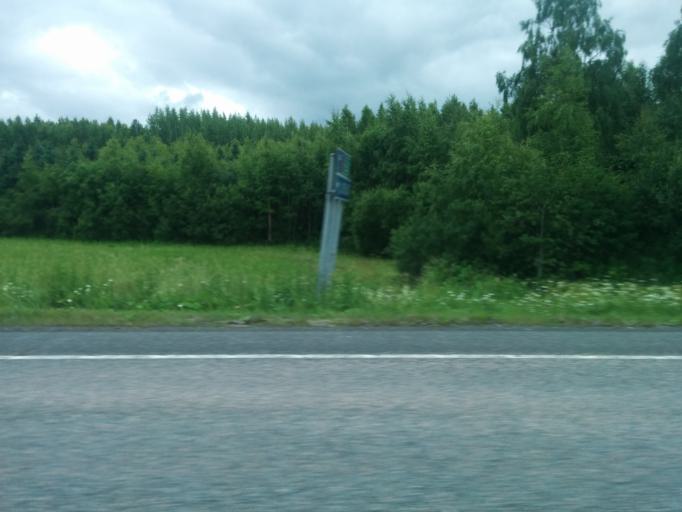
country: FI
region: Pirkanmaa
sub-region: Tampere
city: Orivesi
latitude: 61.7057
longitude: 24.4486
